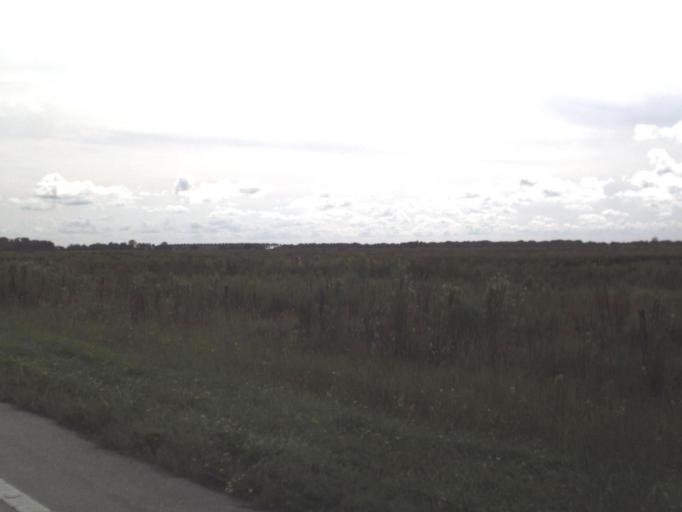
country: US
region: Florida
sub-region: Highlands County
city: Placid Lakes
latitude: 27.2092
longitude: -81.5534
